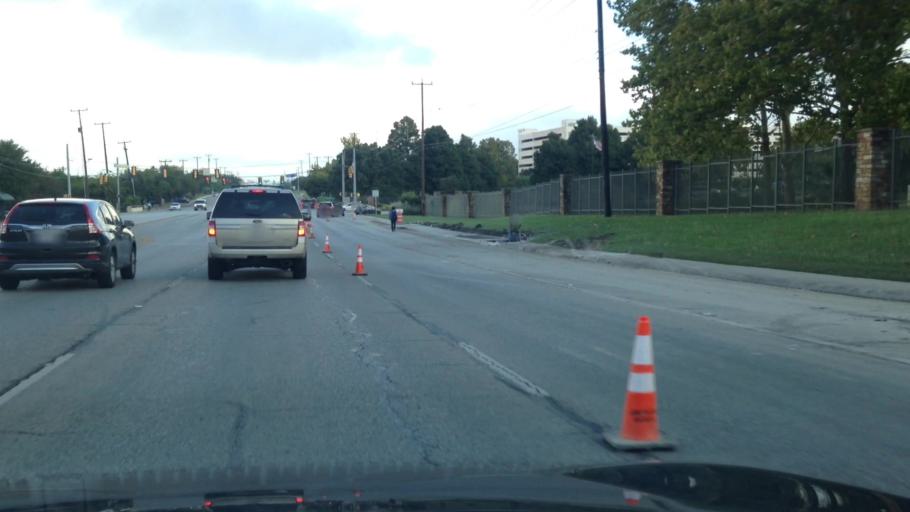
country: US
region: Texas
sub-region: Bexar County
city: Shavano Park
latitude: 29.5364
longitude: -98.5777
